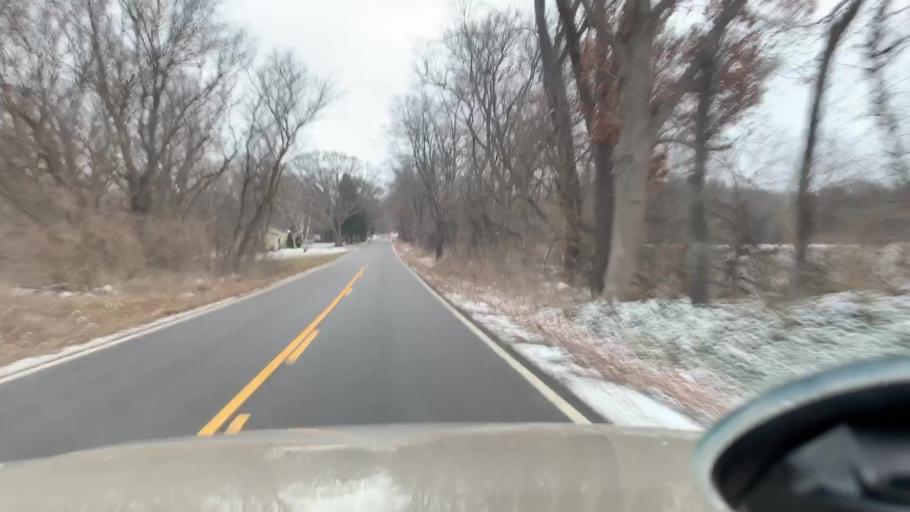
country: US
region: Michigan
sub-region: Jackson County
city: Spring Arbor
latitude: 42.2062
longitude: -84.5309
